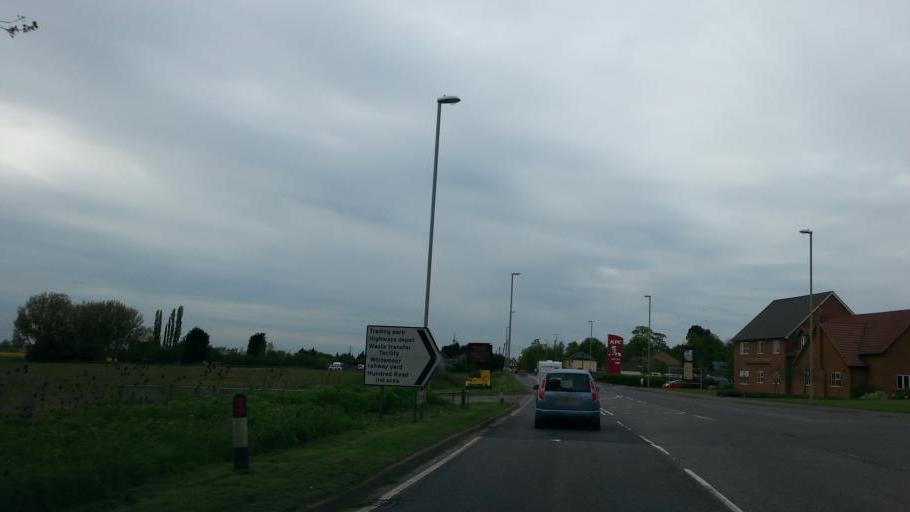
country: GB
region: England
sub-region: Cambridgeshire
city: March
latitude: 52.5618
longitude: 0.0653
